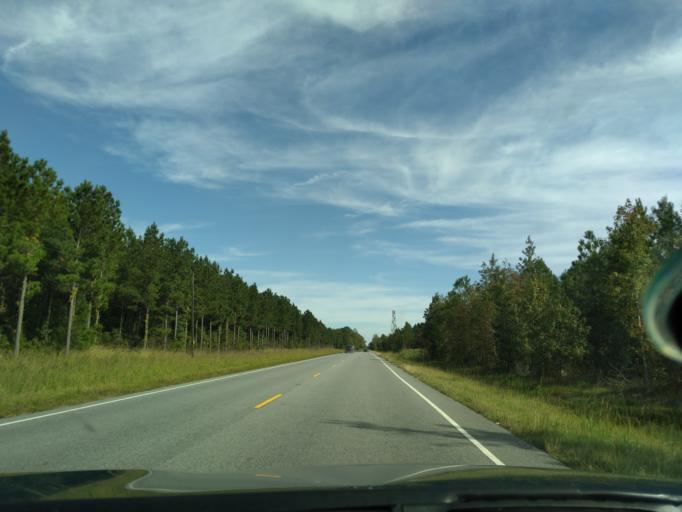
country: US
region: North Carolina
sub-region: Beaufort County
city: River Road
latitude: 35.5252
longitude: -76.8649
